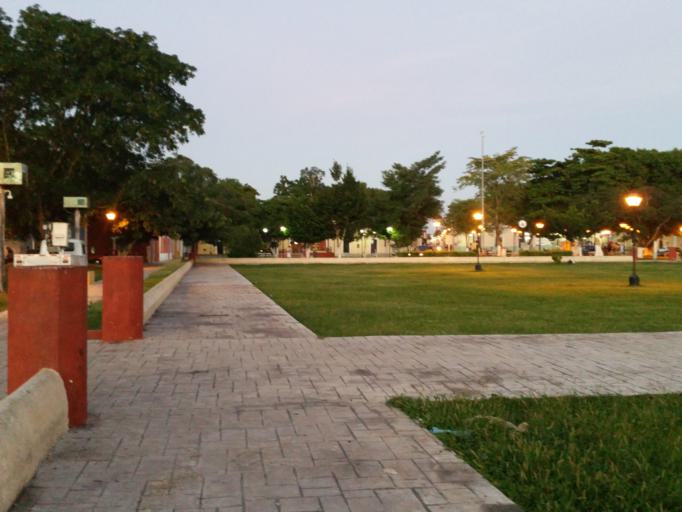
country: MX
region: Yucatan
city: Valladolid
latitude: 20.6861
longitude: -88.2106
